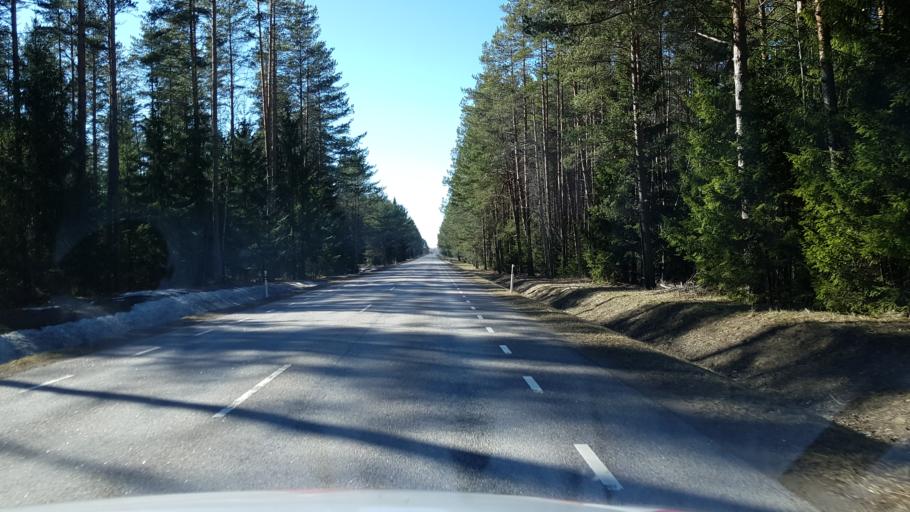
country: EE
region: Laeaene-Virumaa
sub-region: Viru-Nigula vald
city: Kunda
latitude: 59.3581
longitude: 26.6437
